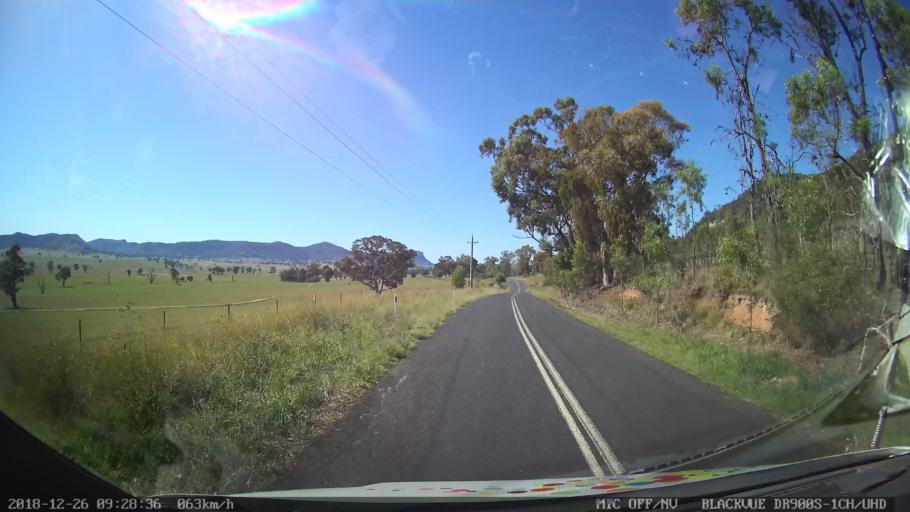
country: AU
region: New South Wales
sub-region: Mid-Western Regional
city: Kandos
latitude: -32.8459
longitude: 150.0224
